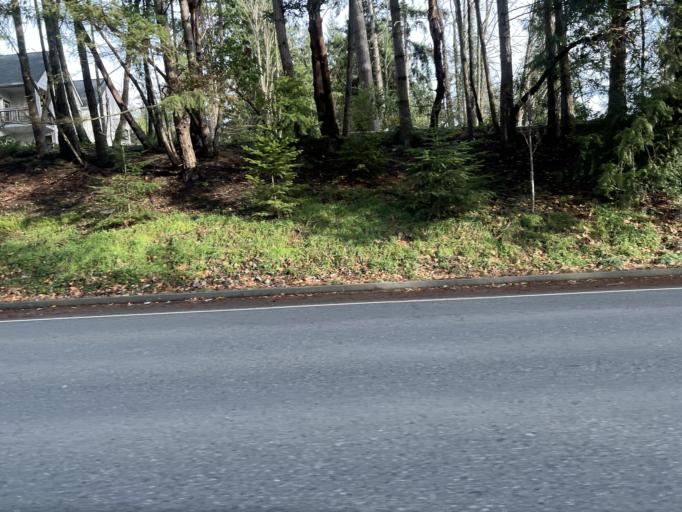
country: US
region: Washington
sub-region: Kitsap County
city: Bainbridge Island
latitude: 47.6269
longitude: -122.5120
